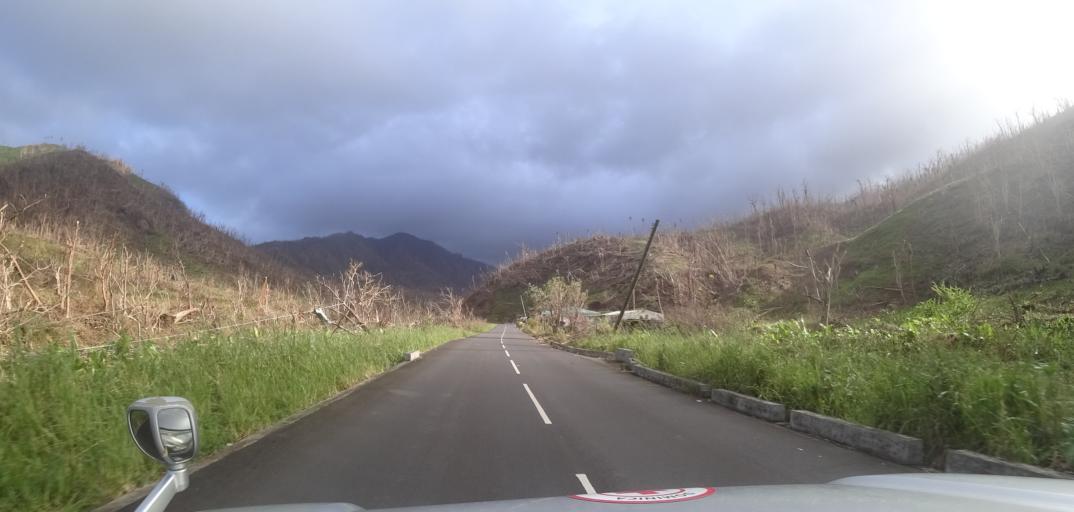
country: DM
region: Saint Andrew
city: Marigot
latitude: 15.4973
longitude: -61.2769
